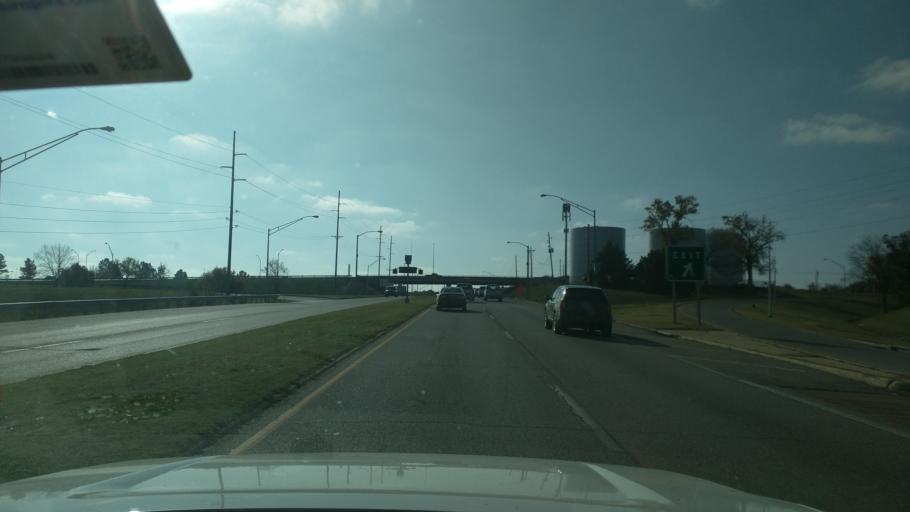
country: US
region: Oklahoma
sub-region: Washington County
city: Bartlesville
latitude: 36.7449
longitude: -95.9354
